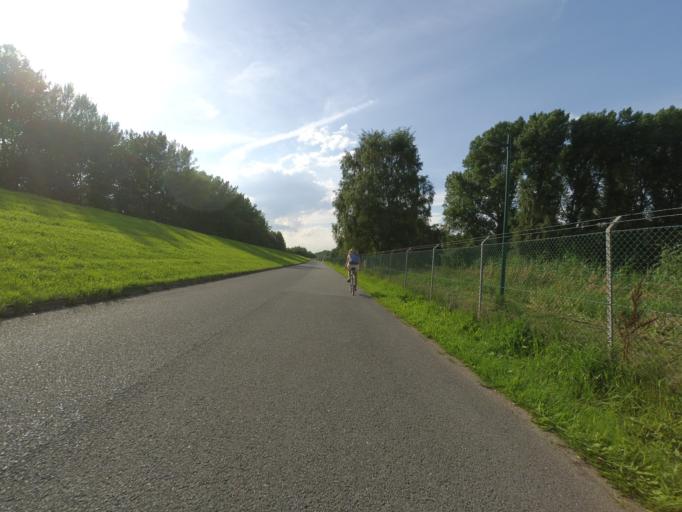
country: DE
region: Hamburg
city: Rothenburgsort
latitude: 53.5260
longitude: 10.0485
